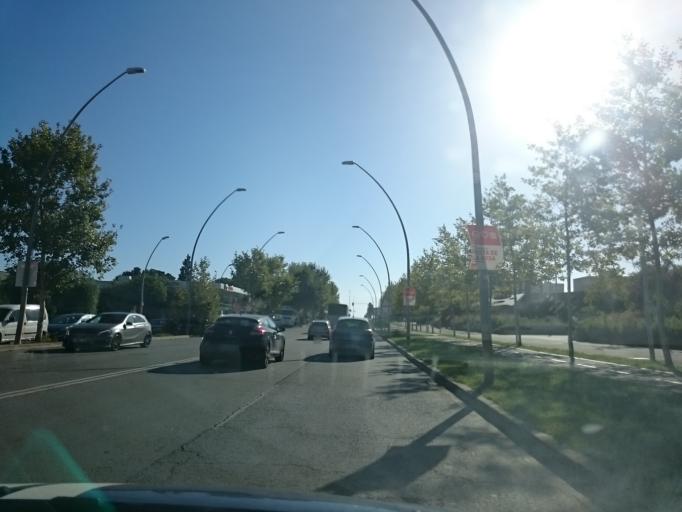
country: ES
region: Catalonia
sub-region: Provincia de Barcelona
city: Sant Boi de Llobregat
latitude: 41.3342
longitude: 2.0448
